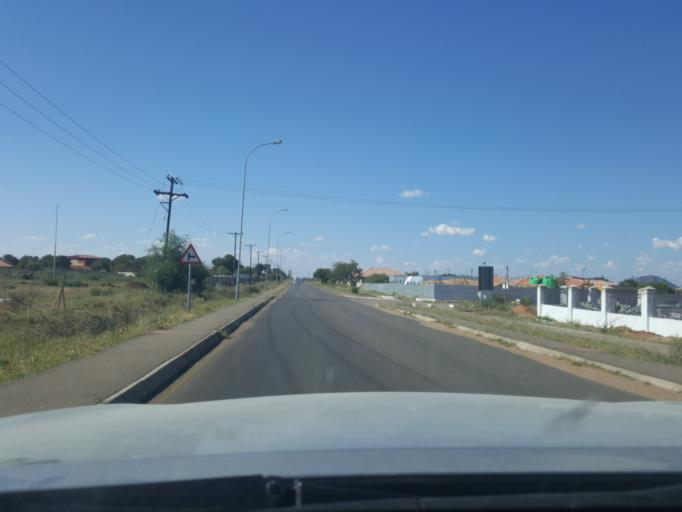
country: BW
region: South East
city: Gaborone
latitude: -24.6144
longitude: 25.9490
